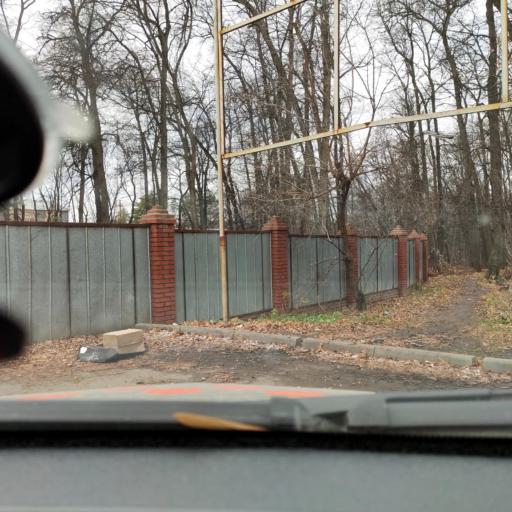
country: RU
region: Bashkortostan
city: Ufa
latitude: 54.7731
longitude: 56.0131
